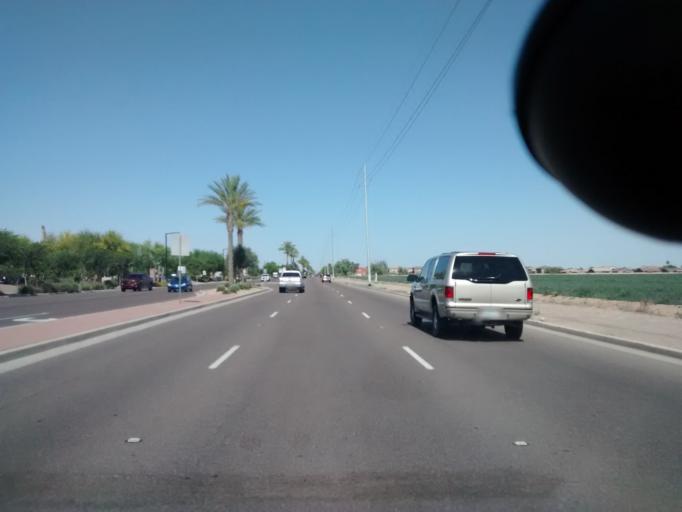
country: US
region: Arizona
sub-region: Maricopa County
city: Peoria
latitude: 33.5376
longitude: -112.2544
